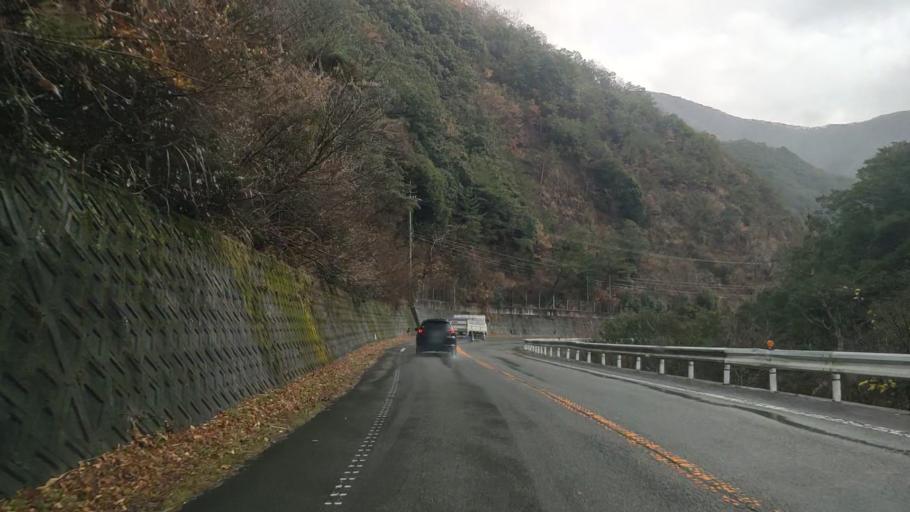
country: JP
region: Tokushima
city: Kamojimacho-jogejima
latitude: 34.1629
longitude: 134.3523
